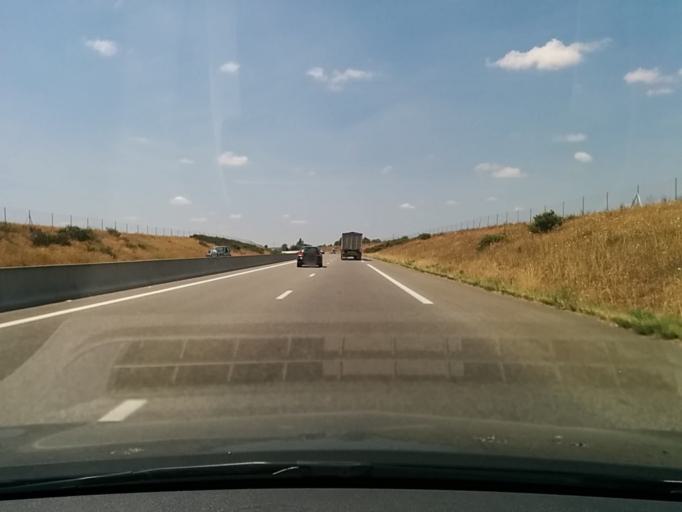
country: FR
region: Midi-Pyrenees
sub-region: Departement de la Haute-Garonne
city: La Salvetat-Saint-Gilles
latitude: 43.5854
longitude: 1.2607
